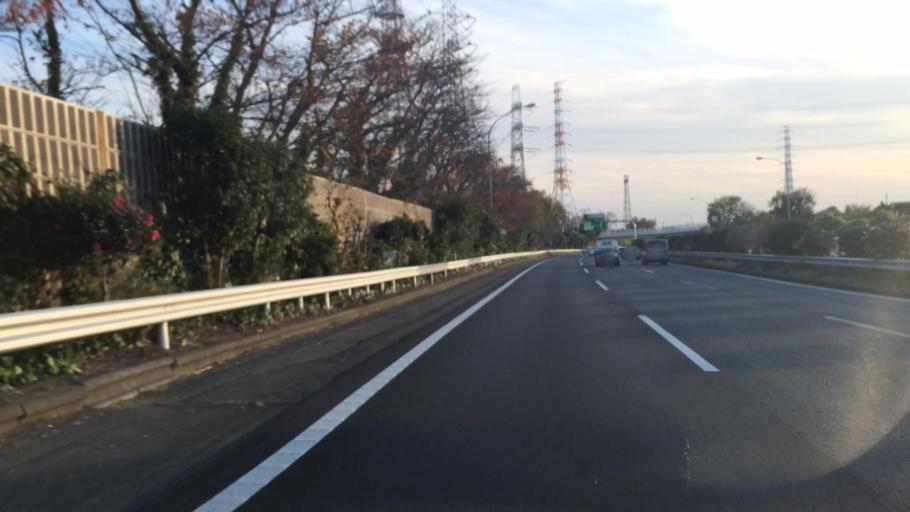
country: JP
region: Kanagawa
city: Yokohama
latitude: 35.5384
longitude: 139.6019
